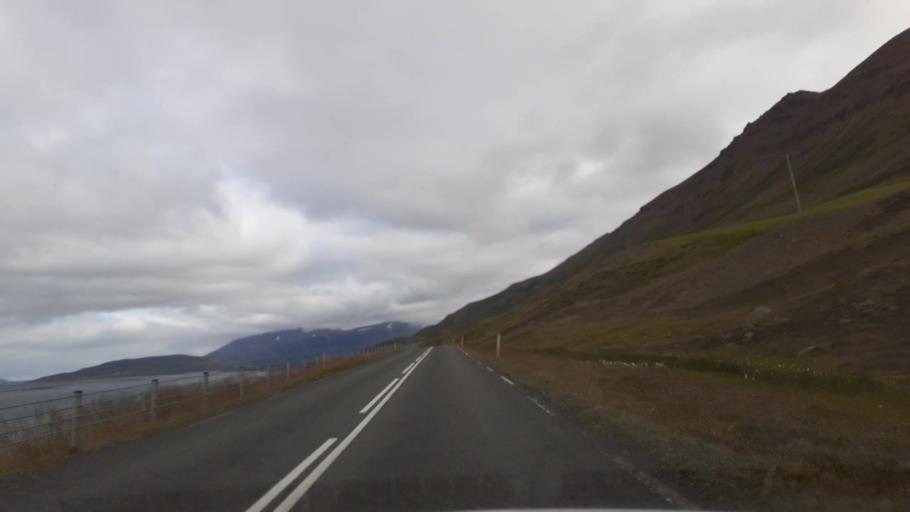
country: IS
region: Northeast
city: Akureyri
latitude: 65.8410
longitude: -18.0566
